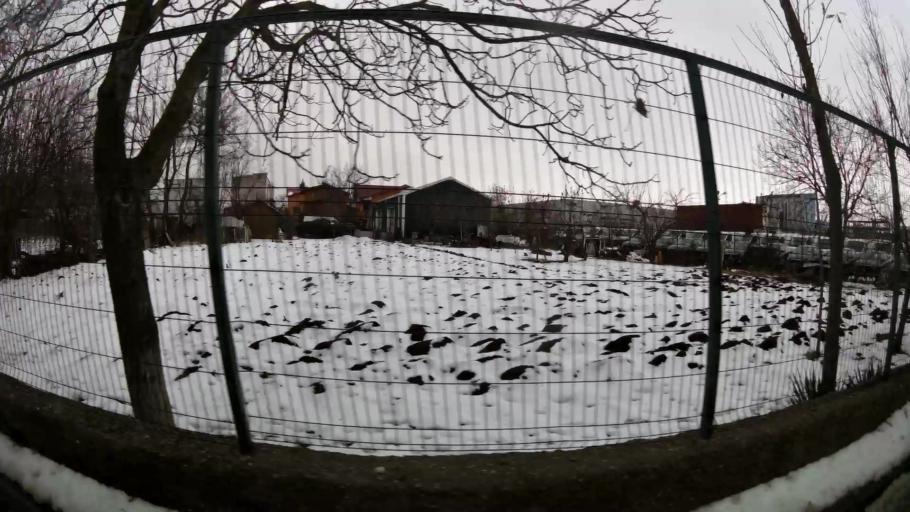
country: RO
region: Ilfov
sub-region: Comuna Otopeni
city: Otopeni
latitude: 44.5421
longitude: 26.0712
